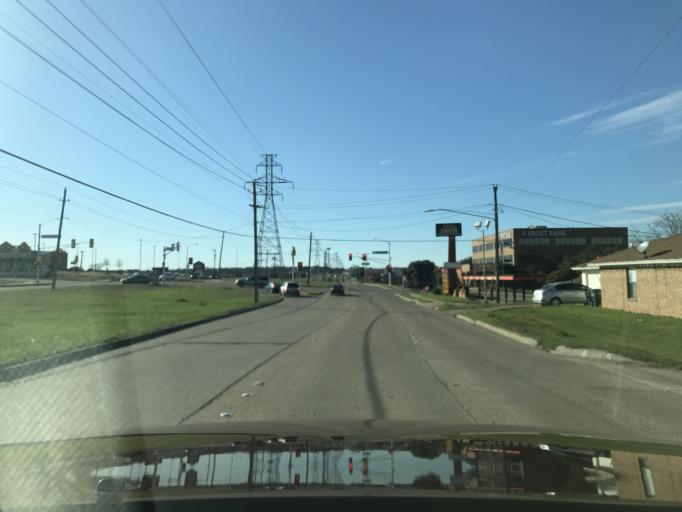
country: US
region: Texas
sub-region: Tarrant County
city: Edgecliff Village
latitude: 32.6492
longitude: -97.3596
